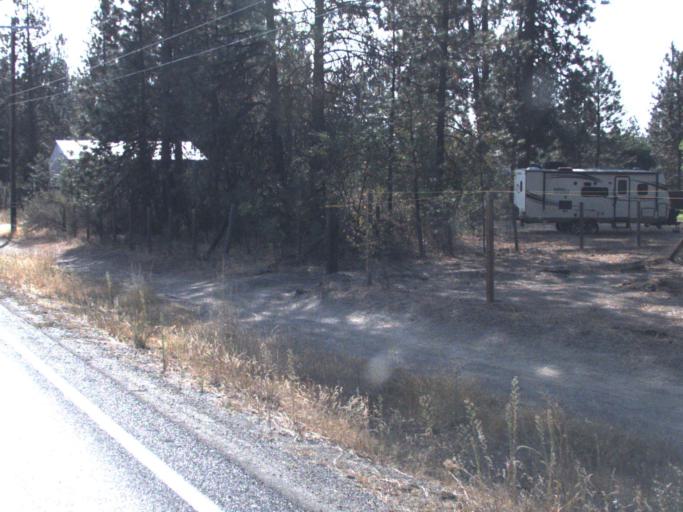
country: US
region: Washington
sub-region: Spokane County
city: Fairwood
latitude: 47.8140
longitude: -117.5746
